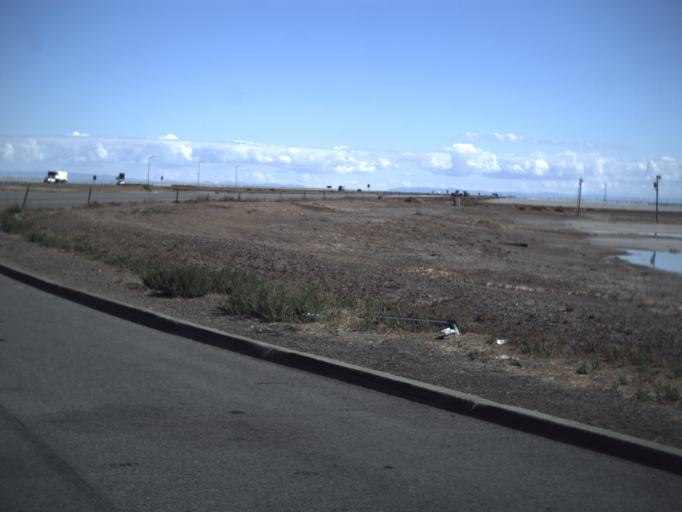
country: US
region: Utah
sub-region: Tooele County
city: Wendover
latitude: 40.7382
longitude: -113.8559
